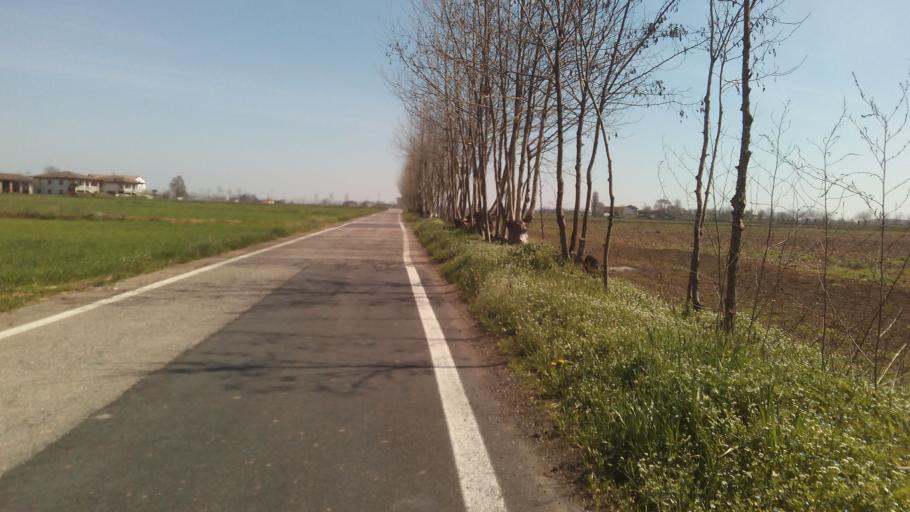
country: IT
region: Lombardy
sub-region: Provincia di Mantova
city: Cerlongo
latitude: 45.2859
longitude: 10.6732
